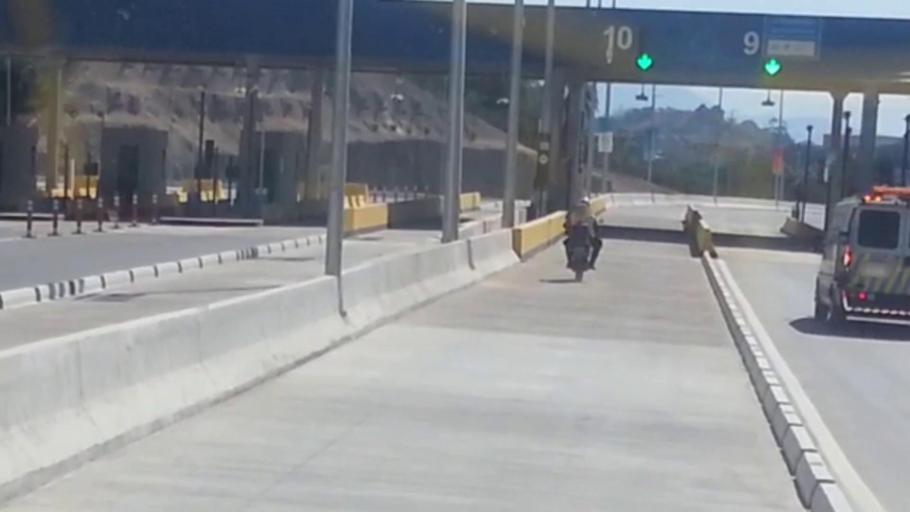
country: BR
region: Rio de Janeiro
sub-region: Nilopolis
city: Nilopolis
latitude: -22.8978
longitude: -43.3985
